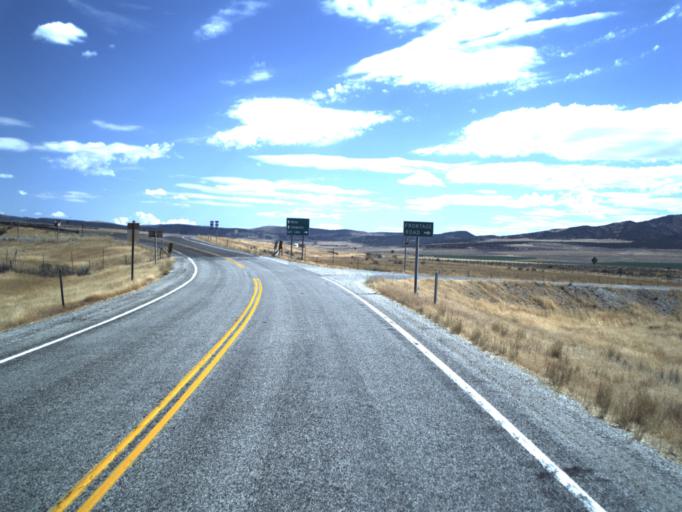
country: US
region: Idaho
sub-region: Oneida County
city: Malad City
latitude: 41.9635
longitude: -112.7620
